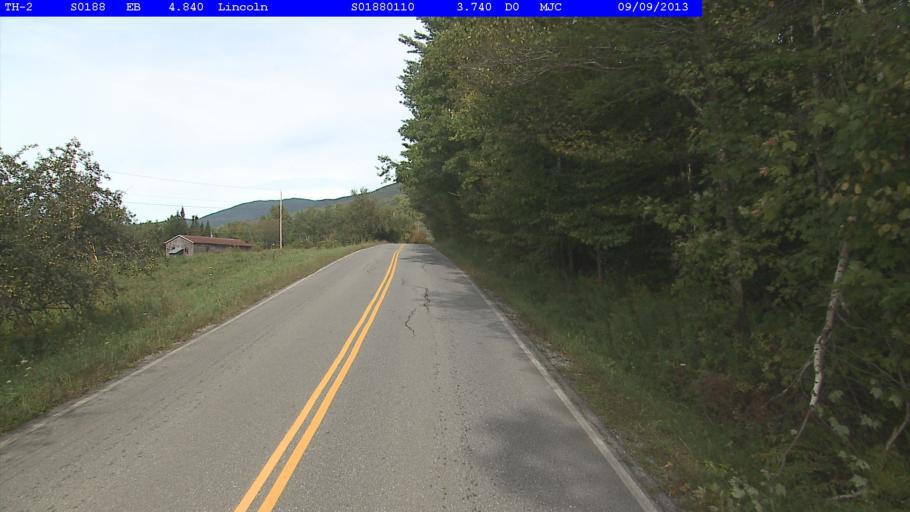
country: US
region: Vermont
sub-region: Addison County
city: Bristol
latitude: 44.0974
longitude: -72.9759
